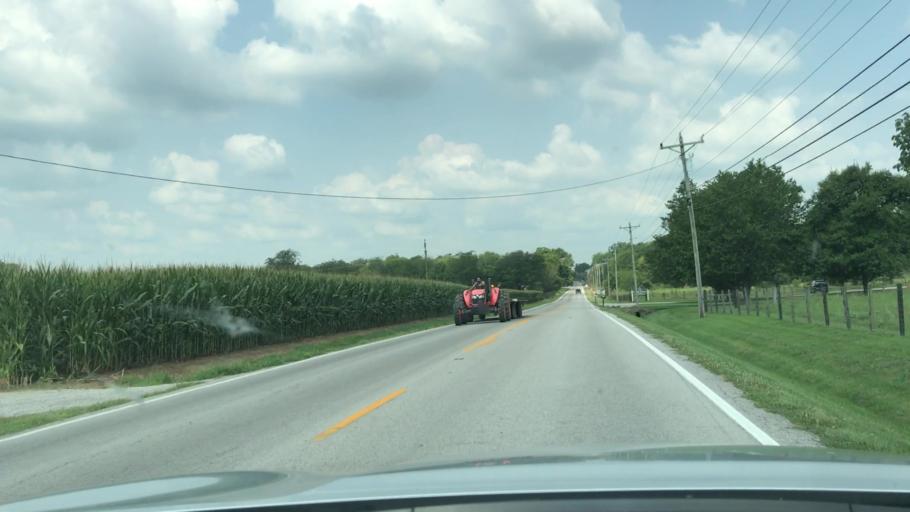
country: US
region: Kentucky
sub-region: Todd County
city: Elkton
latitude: 36.8068
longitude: -87.1365
